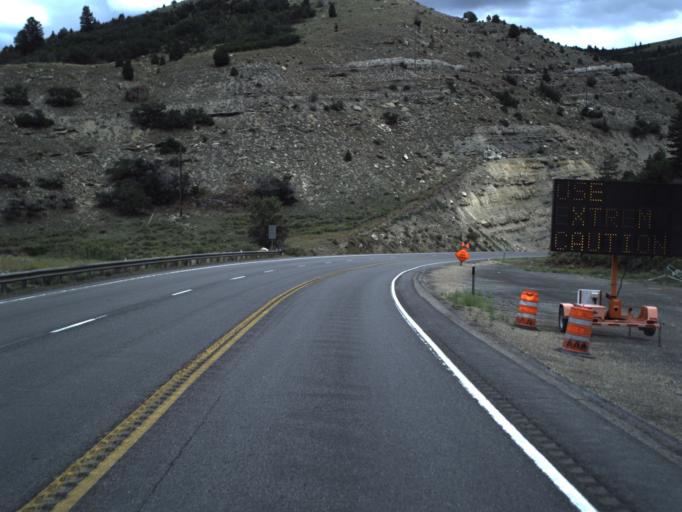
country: US
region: Utah
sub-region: Carbon County
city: Helper
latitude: 39.8007
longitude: -110.9347
